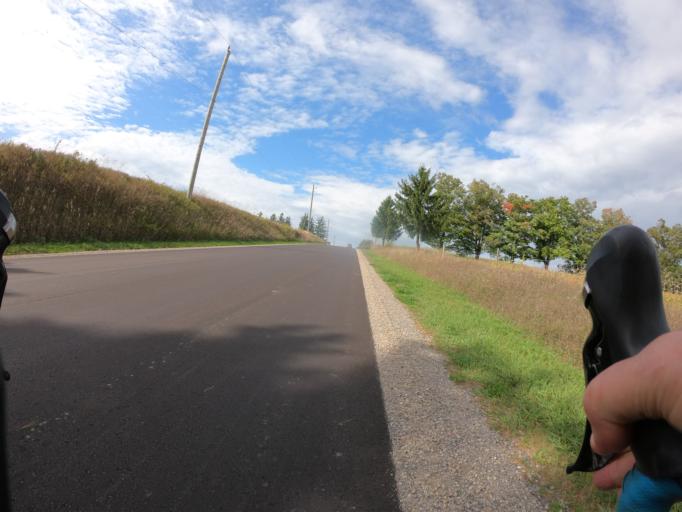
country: CA
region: Ontario
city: Kitchener
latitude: 43.3782
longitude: -80.6193
